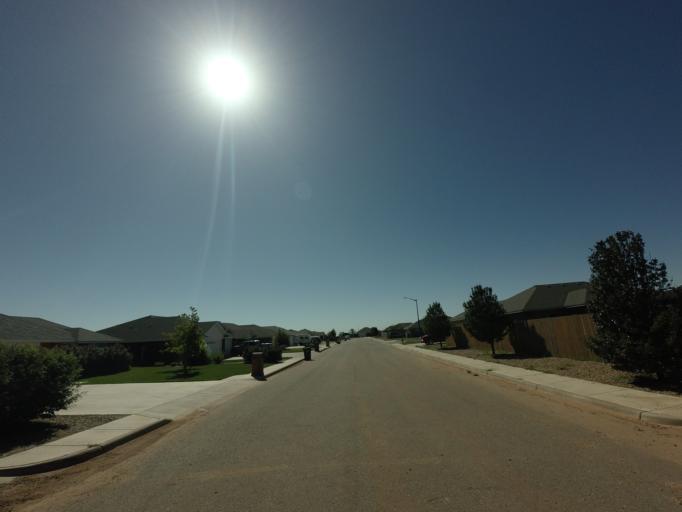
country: US
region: New Mexico
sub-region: Curry County
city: Clovis
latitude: 34.4233
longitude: -103.1569
